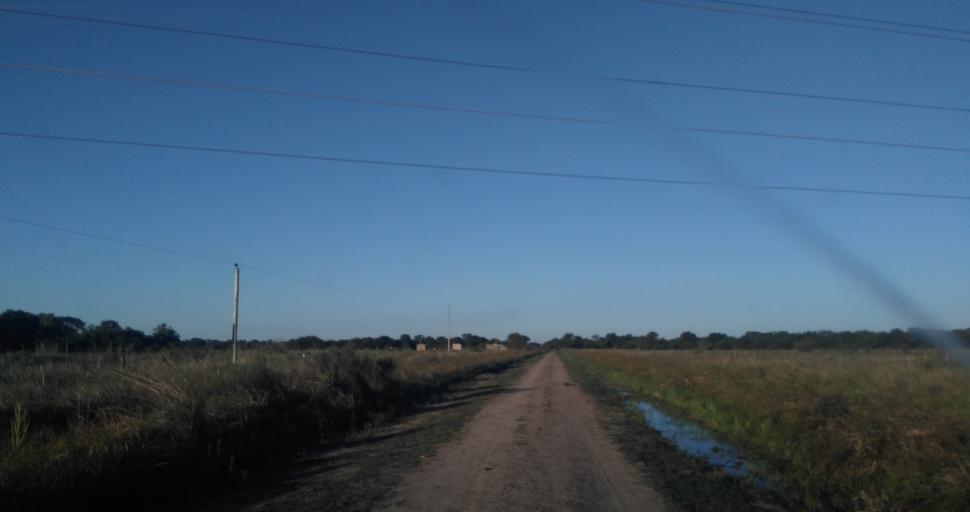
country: AR
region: Chaco
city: Fontana
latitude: -27.3891
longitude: -58.9765
